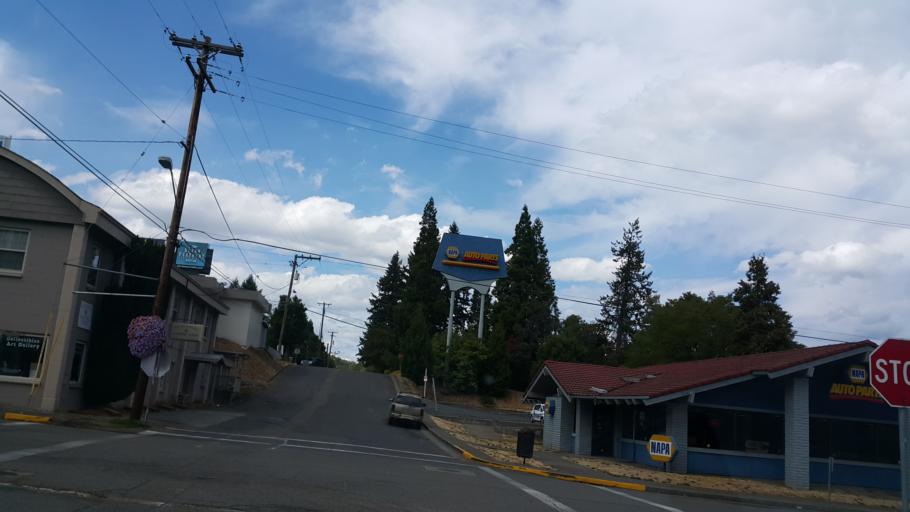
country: US
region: Oregon
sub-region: Douglas County
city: Canyonville
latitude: 42.9250
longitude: -123.2782
